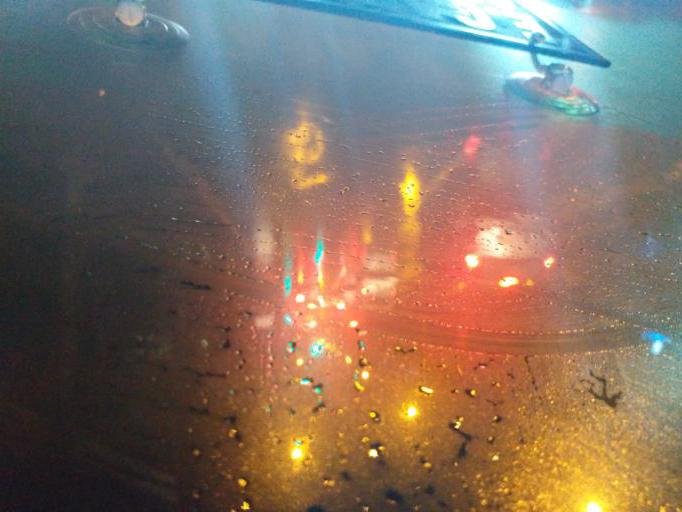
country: TR
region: Ankara
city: Ankara
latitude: 39.9645
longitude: 32.8207
